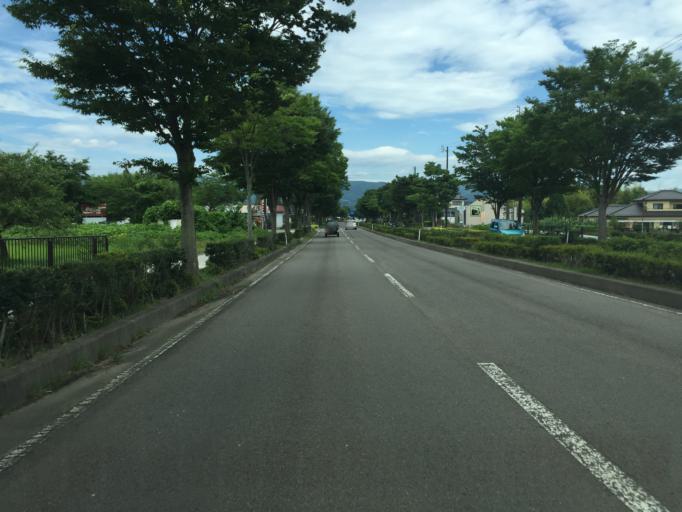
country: JP
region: Fukushima
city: Fukushima-shi
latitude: 37.7377
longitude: 140.3841
